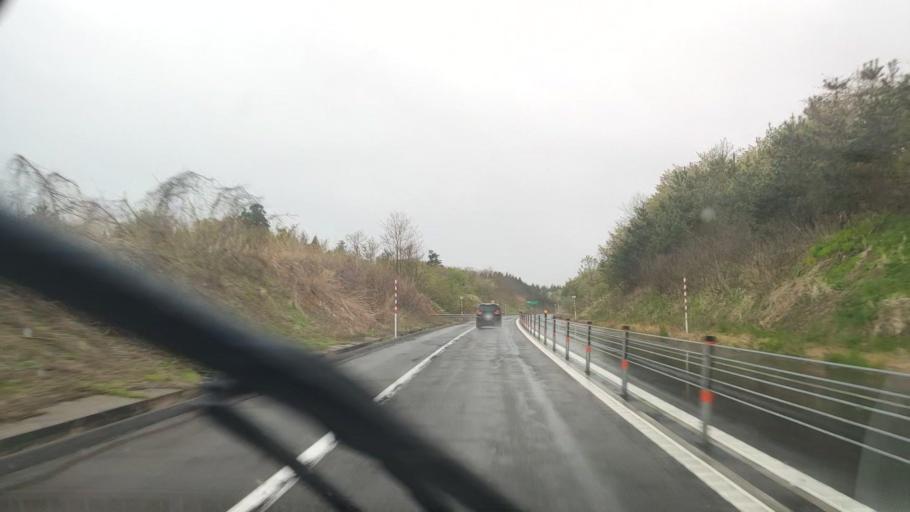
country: JP
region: Akita
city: Noshiromachi
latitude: 40.1649
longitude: 140.0470
